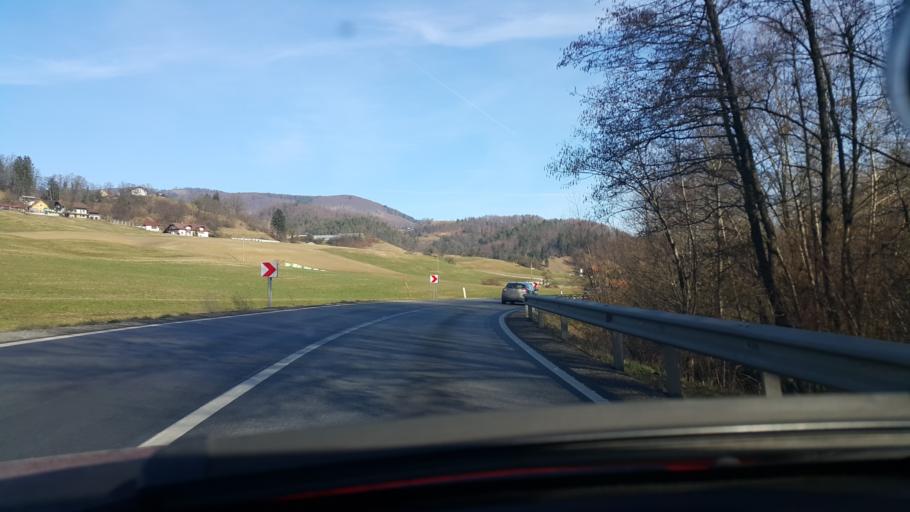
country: SI
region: Zalec
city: Gotovlje
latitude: 46.3185
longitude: 15.1769
